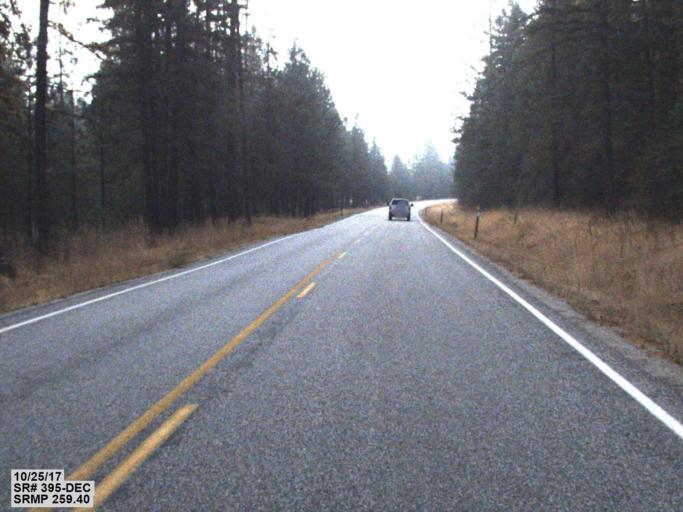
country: US
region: Washington
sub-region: Stevens County
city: Kettle Falls
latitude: 48.8543
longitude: -118.2028
